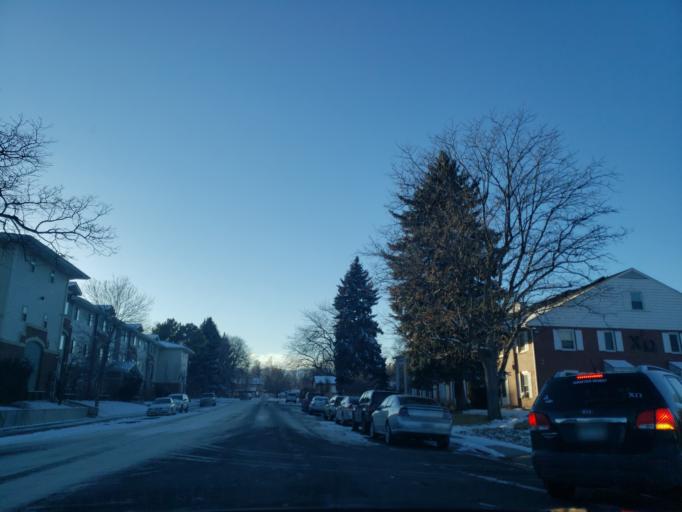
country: US
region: Colorado
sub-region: Larimer County
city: Fort Collins
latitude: 40.5790
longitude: -105.0973
